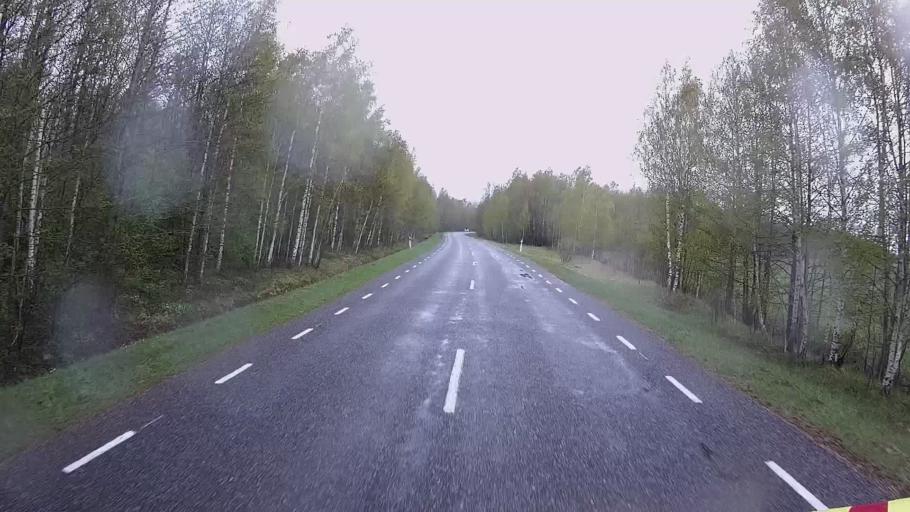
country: EE
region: Hiiumaa
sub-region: Kaerdla linn
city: Kardla
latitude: 58.7286
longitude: 22.5527
